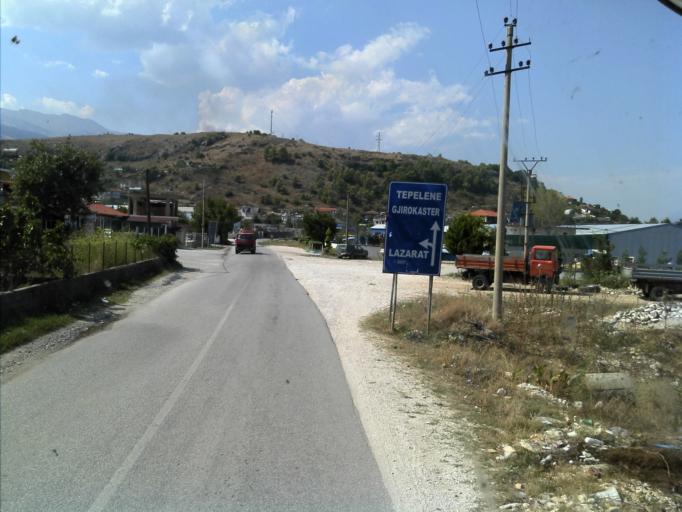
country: AL
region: Gjirokaster
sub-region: Rrethi i Gjirokastres
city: Dervician
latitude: 40.0558
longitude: 20.1750
